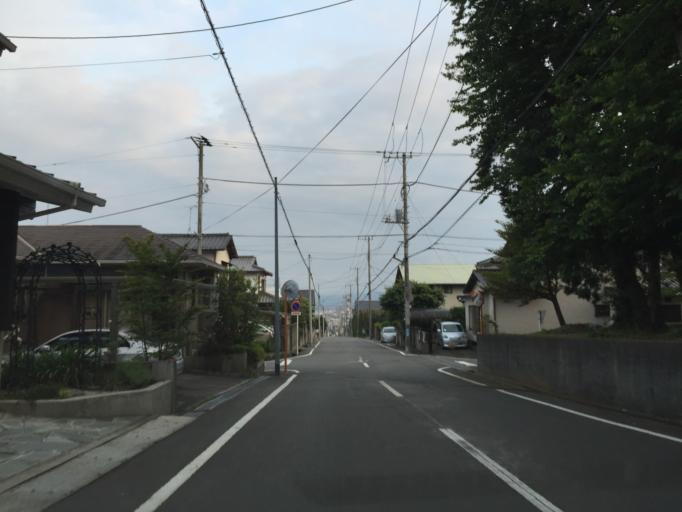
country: JP
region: Shizuoka
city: Numazu
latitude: 35.1313
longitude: 138.8578
